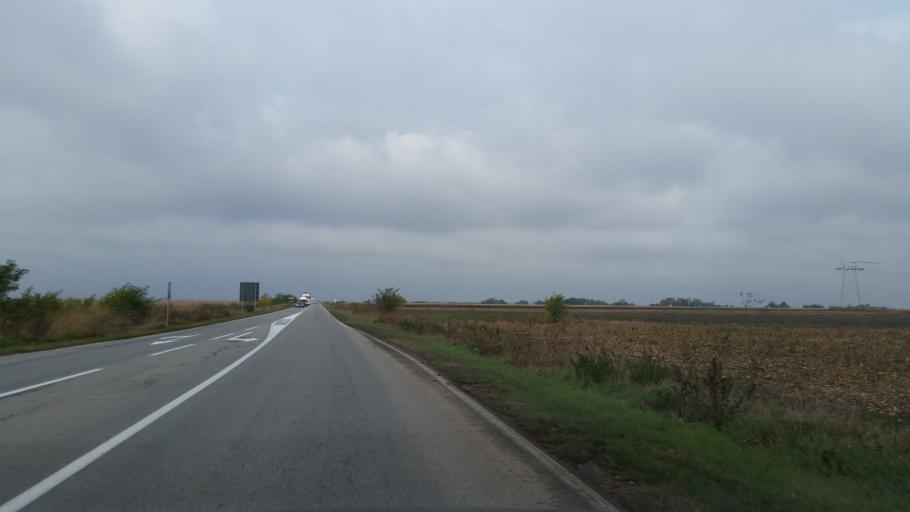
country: RS
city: Elemir
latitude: 45.4601
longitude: 20.3493
